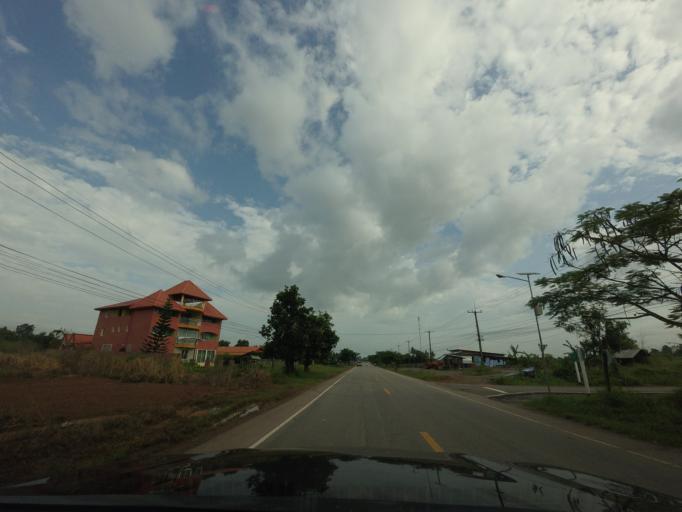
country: TH
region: Nong Khai
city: Pho Tak
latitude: 17.7703
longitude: 102.3962
